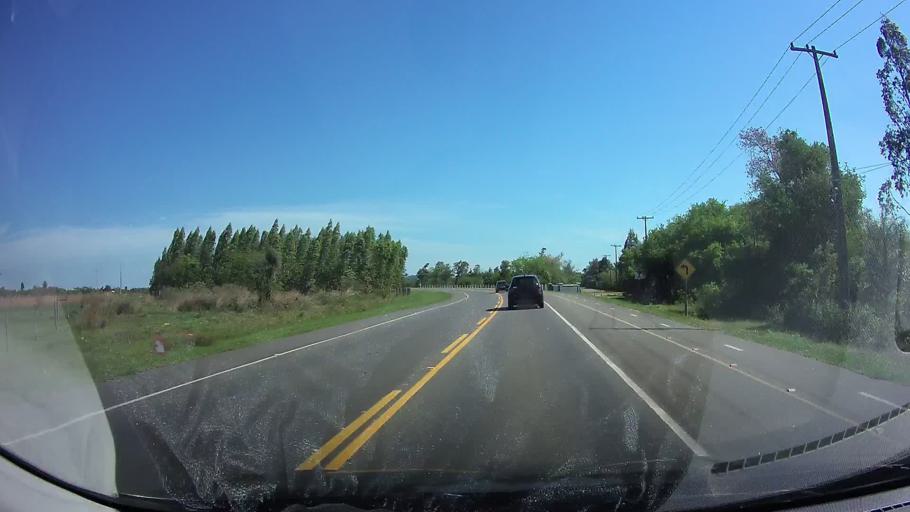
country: PY
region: Cordillera
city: San Bernardino
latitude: -25.2652
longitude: -57.3214
